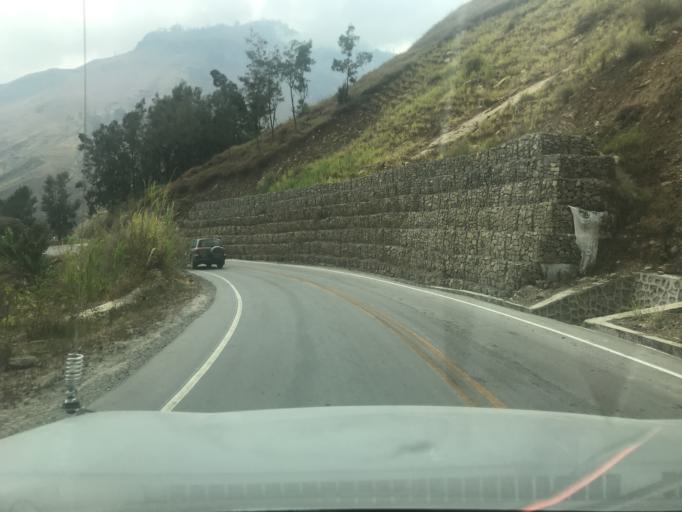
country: TL
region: Manufahi
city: Same
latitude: -8.8919
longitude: 125.5929
